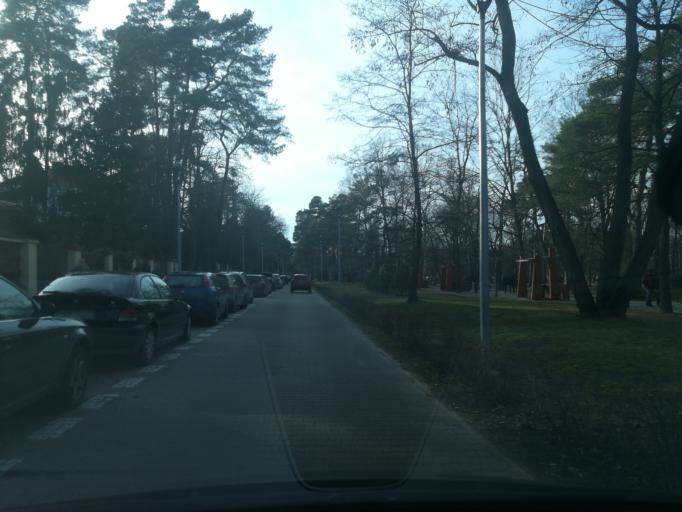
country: PL
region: Masovian Voivodeship
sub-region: Powiat piaseczynski
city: Konstancin-Jeziorna
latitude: 52.0843
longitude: 21.1161
